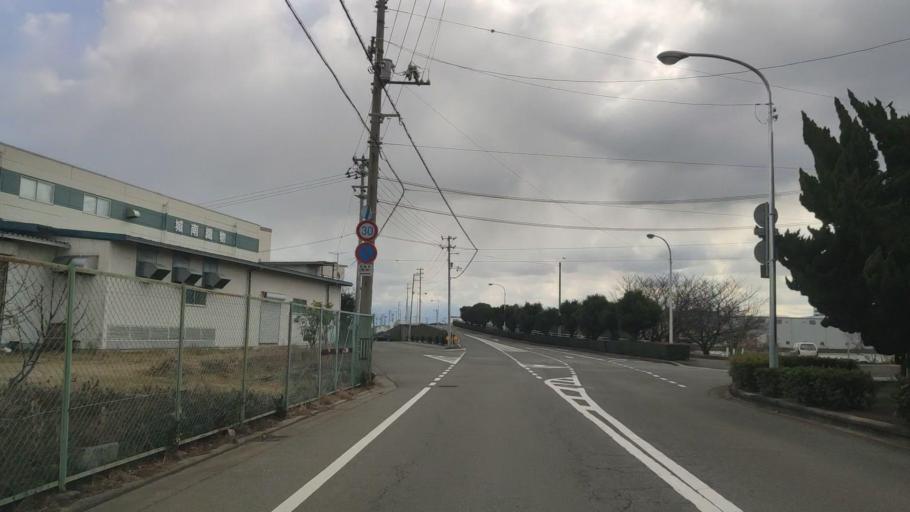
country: JP
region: Ehime
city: Saijo
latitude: 34.0531
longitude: 133.0227
